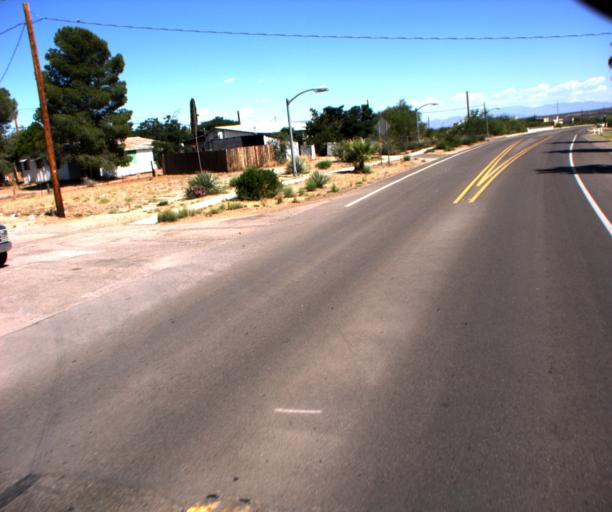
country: US
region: Arizona
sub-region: Pinal County
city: Mammoth
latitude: 32.7347
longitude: -110.6485
